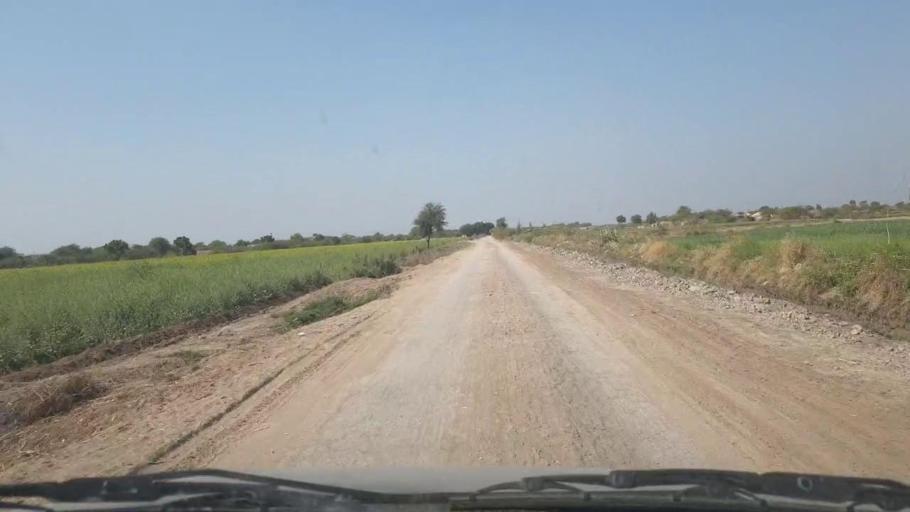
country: PK
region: Sindh
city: Samaro
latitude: 25.2247
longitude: 69.3273
